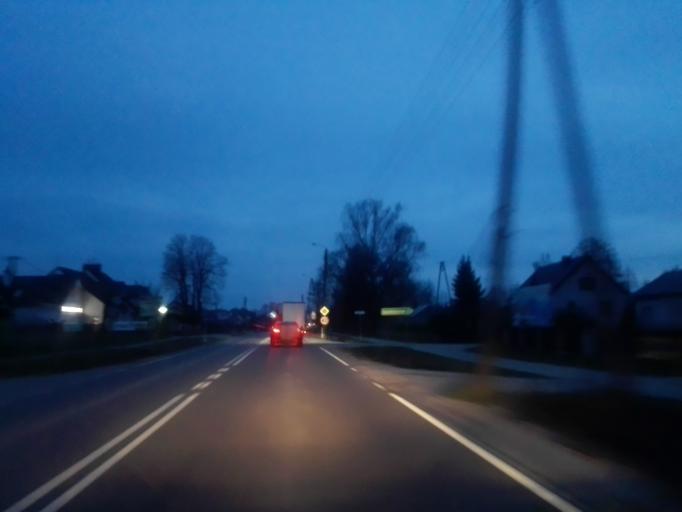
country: PL
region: Podlasie
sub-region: Lomza
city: Lomza
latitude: 53.1387
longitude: 22.0435
